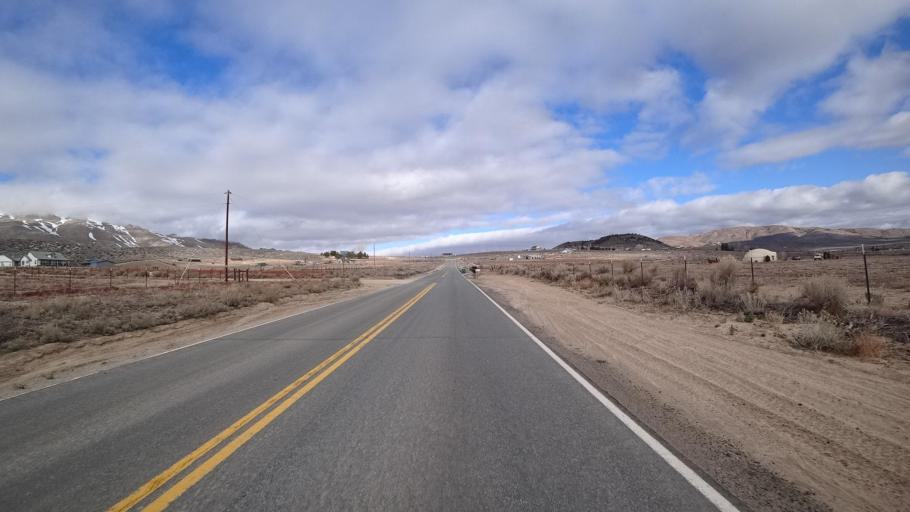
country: US
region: Nevada
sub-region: Washoe County
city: Cold Springs
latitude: 39.8638
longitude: -119.9416
